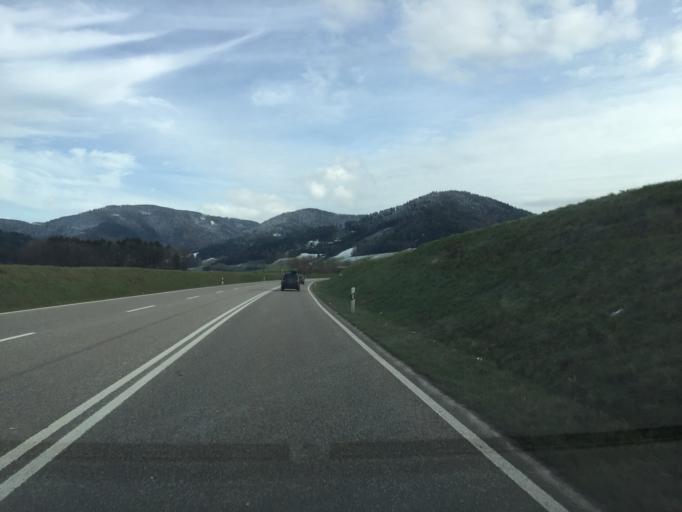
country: DE
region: Baden-Wuerttemberg
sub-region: Freiburg Region
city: Stegen
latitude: 47.9680
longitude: 7.9817
